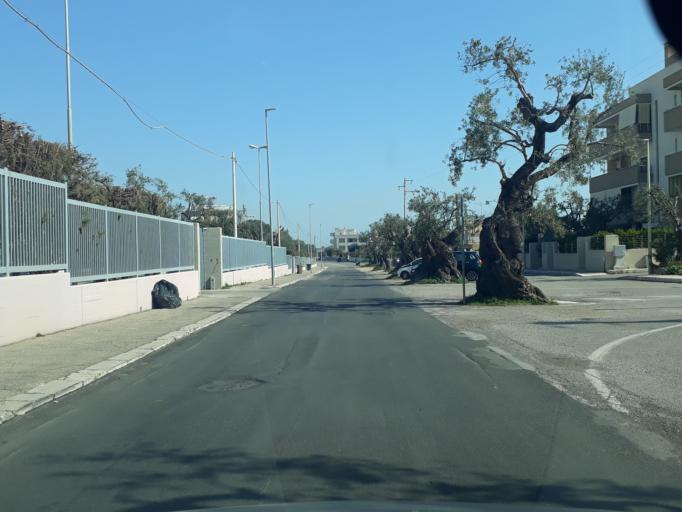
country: IT
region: Apulia
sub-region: Provincia di Brindisi
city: Fasano
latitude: 40.8286
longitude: 17.3646
